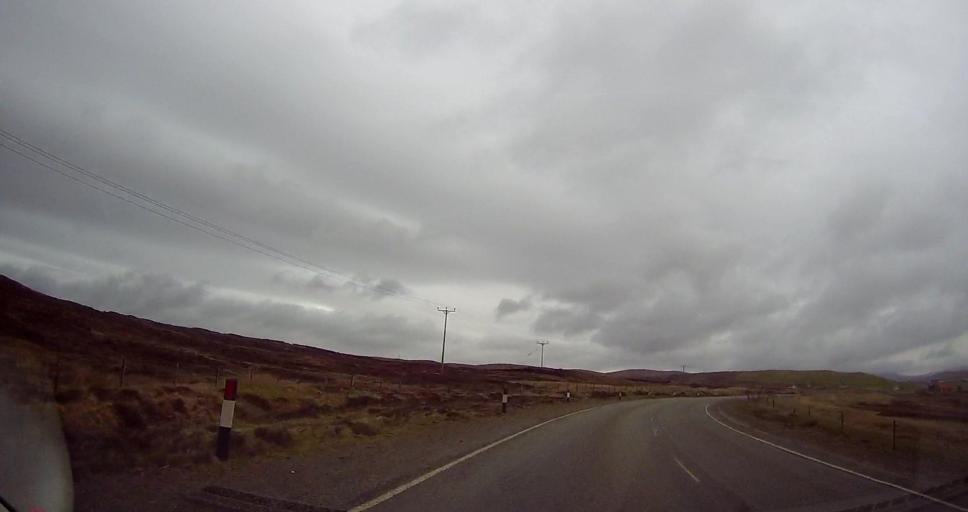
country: GB
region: Scotland
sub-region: Shetland Islands
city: Lerwick
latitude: 60.2286
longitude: -1.2373
